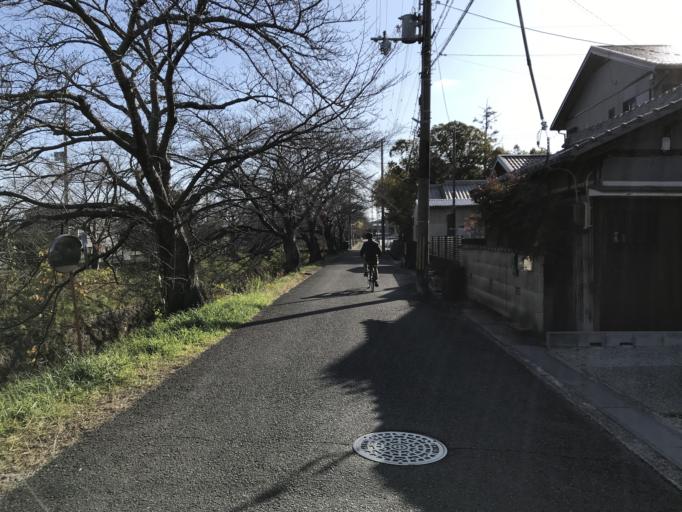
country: JP
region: Kyoto
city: Tanabe
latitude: 34.8194
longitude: 135.7762
